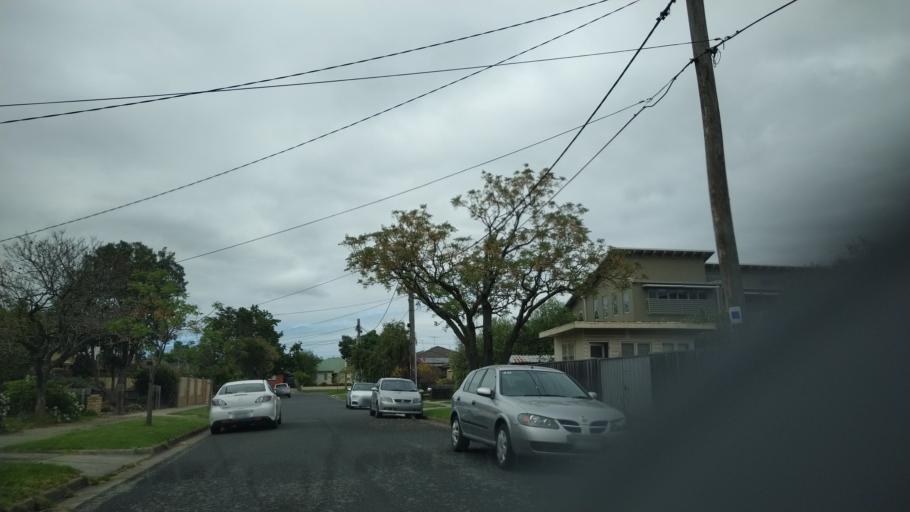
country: AU
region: Victoria
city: Hughesdale
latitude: -37.9099
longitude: 145.0802
